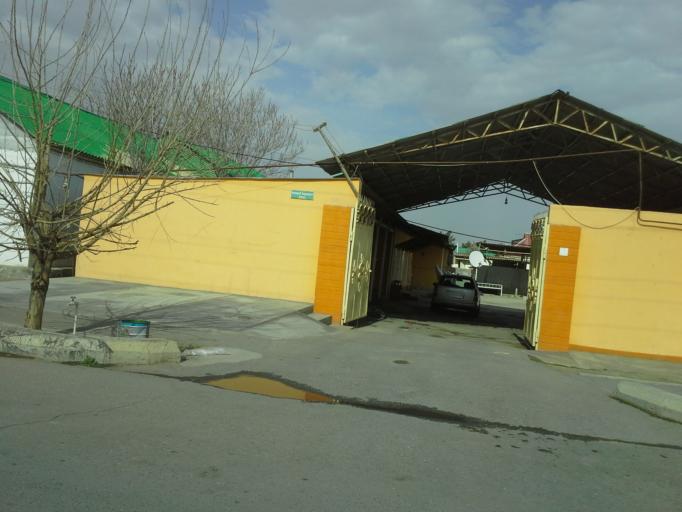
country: TM
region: Ahal
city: Ashgabat
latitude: 37.9858
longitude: 58.2827
